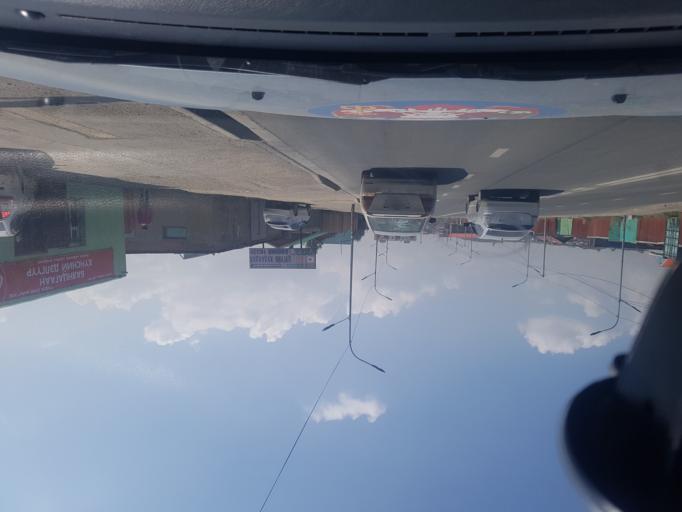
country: MN
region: Ulaanbaatar
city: Ulaanbaatar
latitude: 47.9555
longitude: 106.8332
